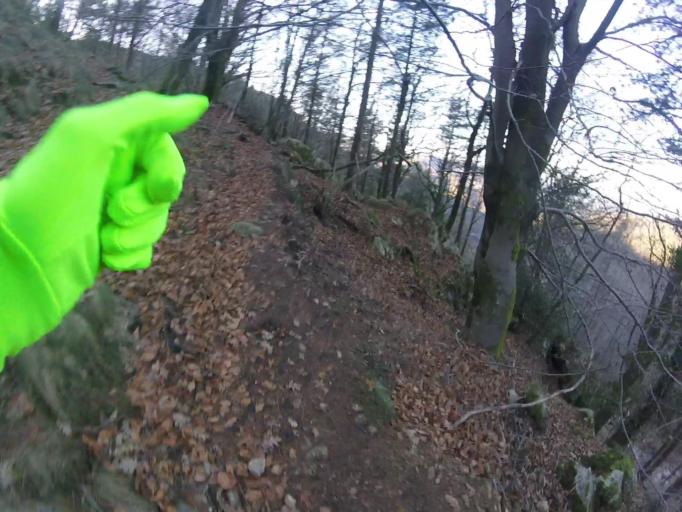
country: ES
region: Basque Country
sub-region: Provincia de Guipuzcoa
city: Irun
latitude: 43.2879
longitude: -1.7916
